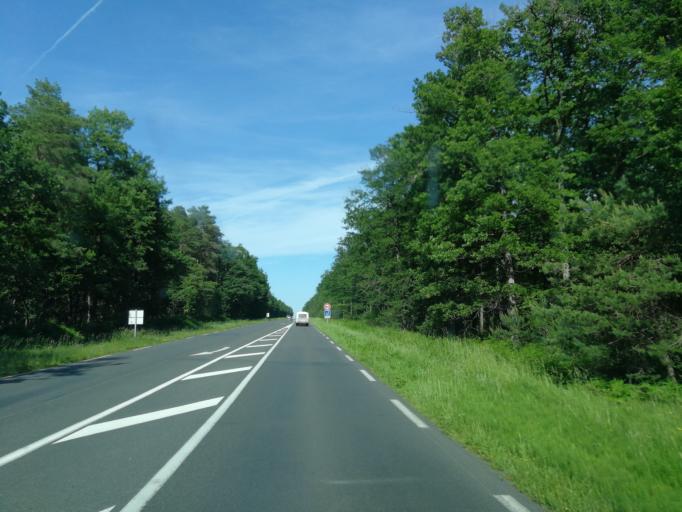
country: FR
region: Centre
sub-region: Departement d'Indre-et-Loire
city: Cheille
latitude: 47.2154
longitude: 0.3601
